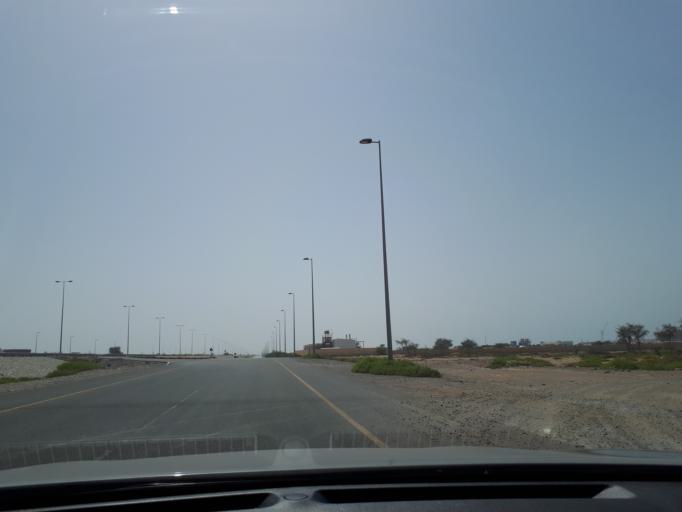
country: OM
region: Al Batinah
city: Barka'
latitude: 23.7001
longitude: 57.9888
